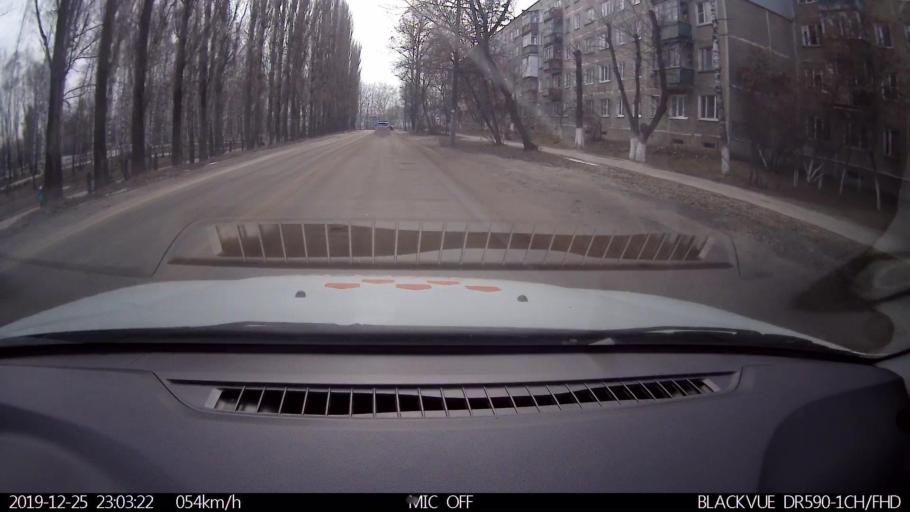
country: RU
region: Nizjnij Novgorod
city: Gorbatovka
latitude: 56.3562
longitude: 43.8209
